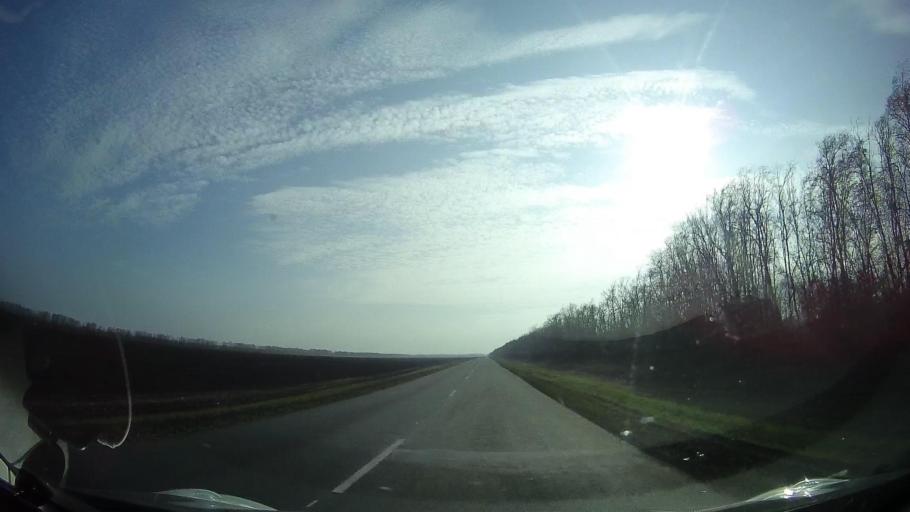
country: RU
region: Rostov
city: Mechetinskaya
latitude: 46.8909
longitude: 40.5419
